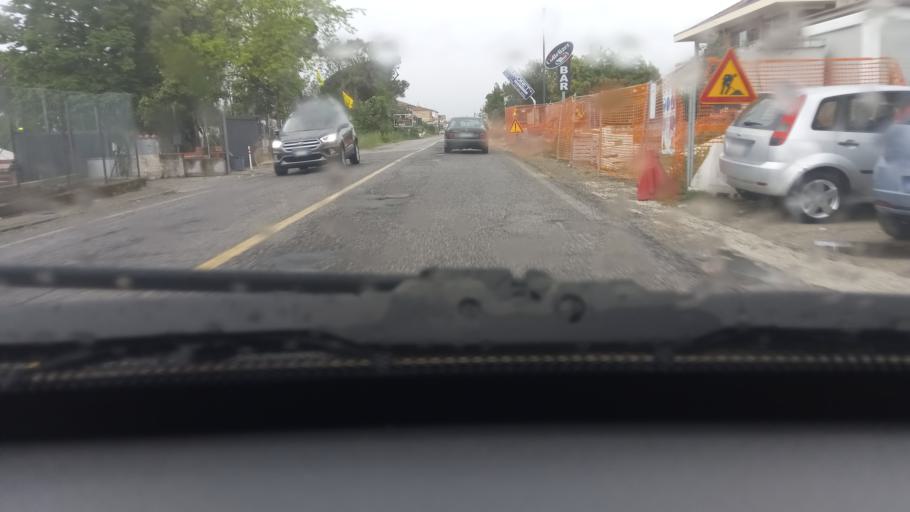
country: IT
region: Latium
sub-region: Provincia di Latina
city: Minturno
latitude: 41.2520
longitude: 13.7273
